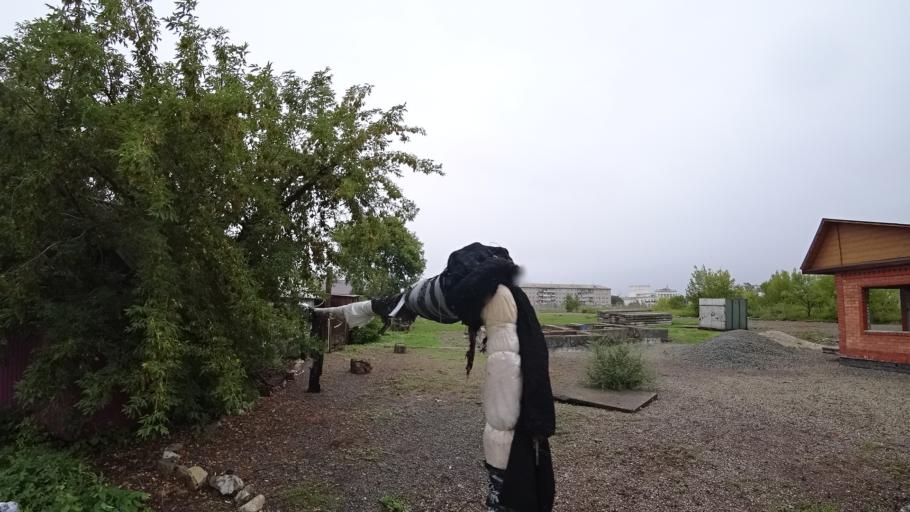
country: RU
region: Primorskiy
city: Monastyrishche
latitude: 44.1972
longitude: 132.4232
